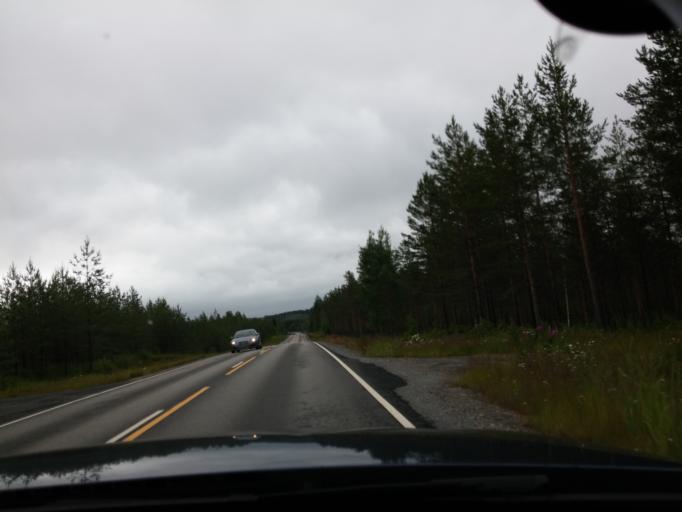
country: FI
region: Central Finland
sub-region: Saarijaervi-Viitasaari
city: Pylkoenmaeki
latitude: 62.6403
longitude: 24.8605
